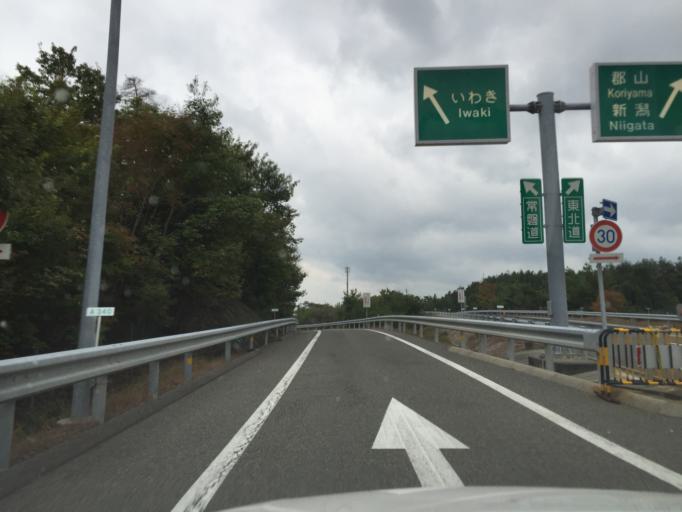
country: JP
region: Fukushima
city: Miharu
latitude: 37.4400
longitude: 140.5230
